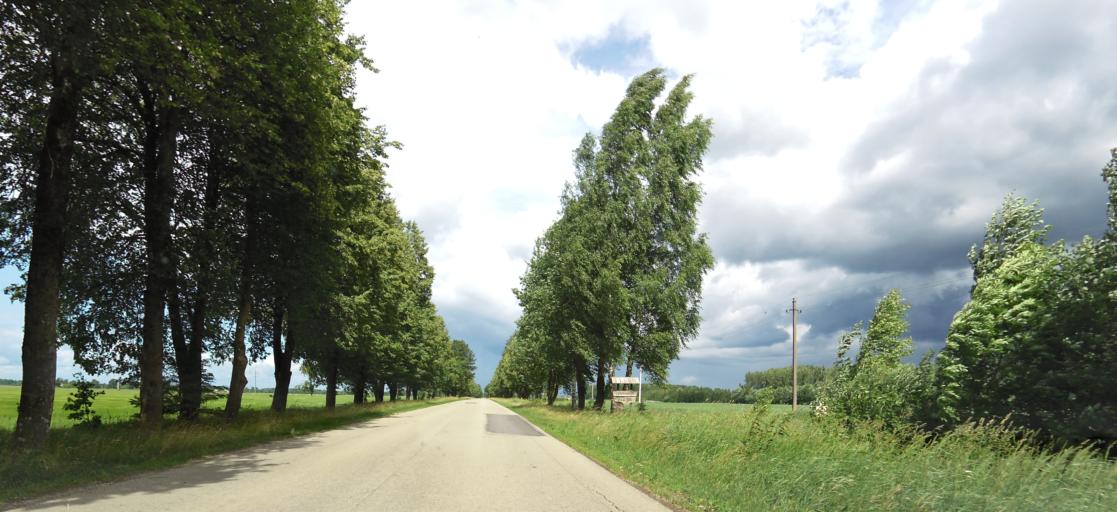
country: LT
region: Panevezys
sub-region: Birzai
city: Birzai
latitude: 56.3593
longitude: 24.7879
